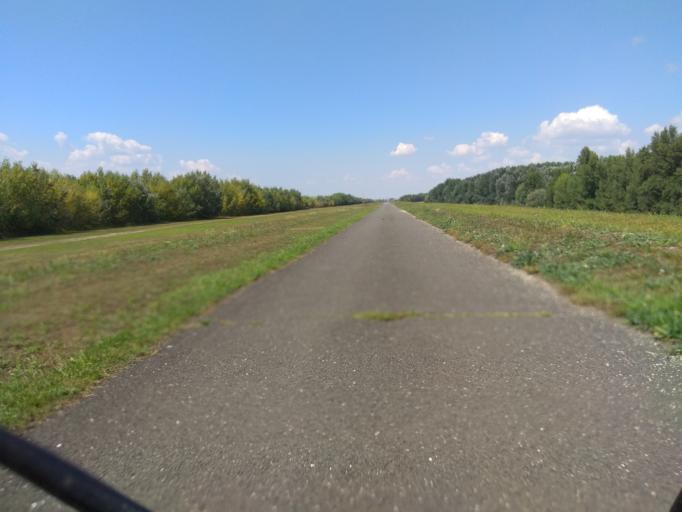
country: SK
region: Trnavsky
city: Gabcikovo
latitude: 47.8504
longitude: 17.5771
